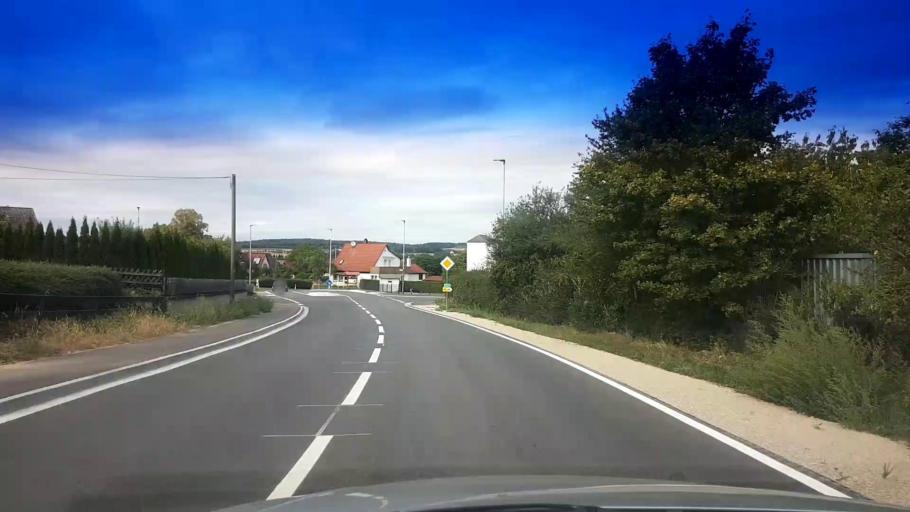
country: DE
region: Bavaria
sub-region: Upper Franconia
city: Frensdorf
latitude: 49.8137
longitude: 10.8716
